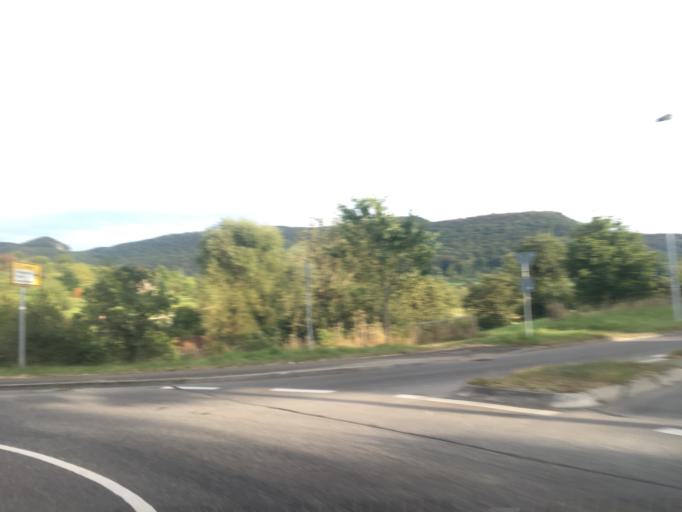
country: DE
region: Baden-Wuerttemberg
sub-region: Tuebingen Region
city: Eningen unter Achalm
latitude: 48.4955
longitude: 9.2646
